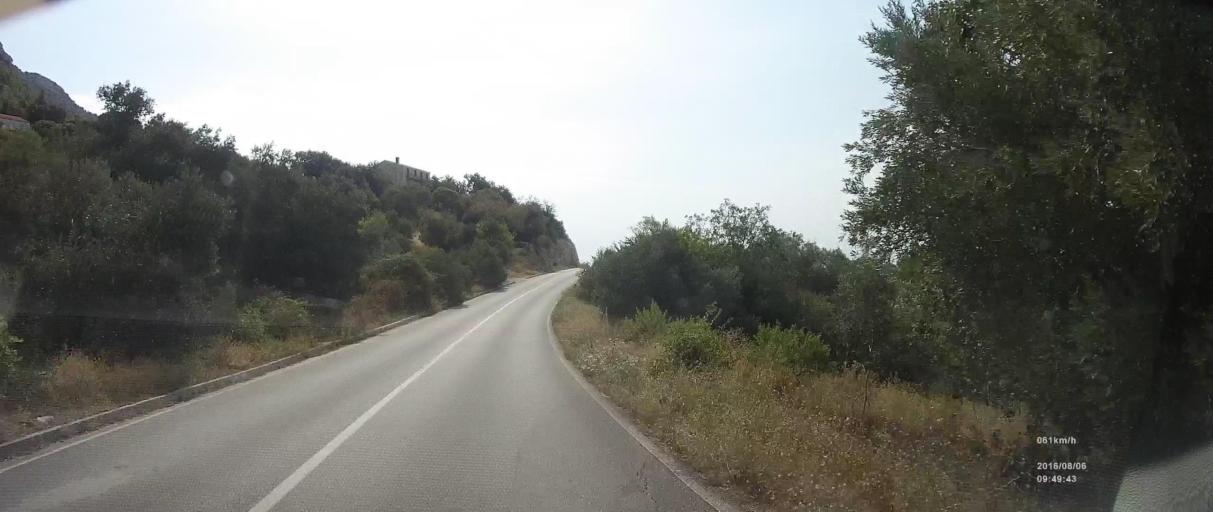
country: HR
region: Dubrovacko-Neretvanska
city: Blato
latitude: 42.7363
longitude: 17.5446
